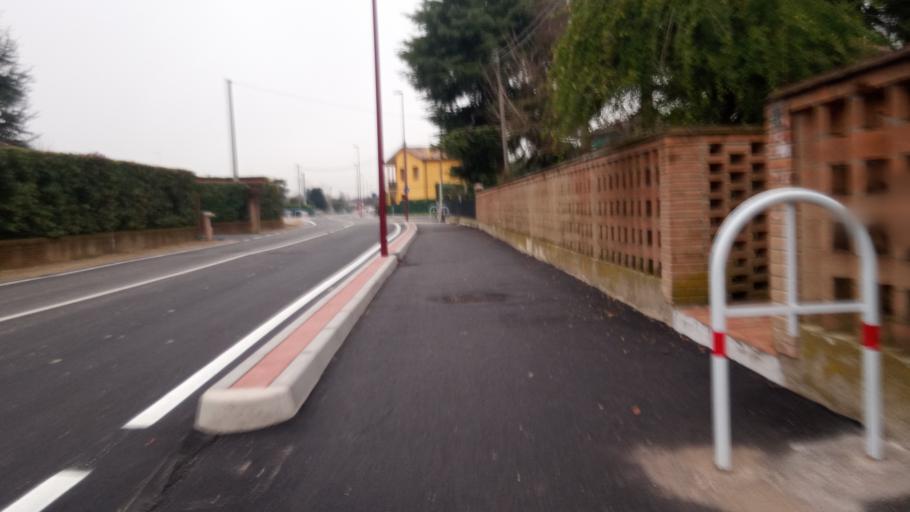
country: IT
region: Veneto
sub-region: Provincia di Padova
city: Sarmeola
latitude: 45.4274
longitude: 11.8231
